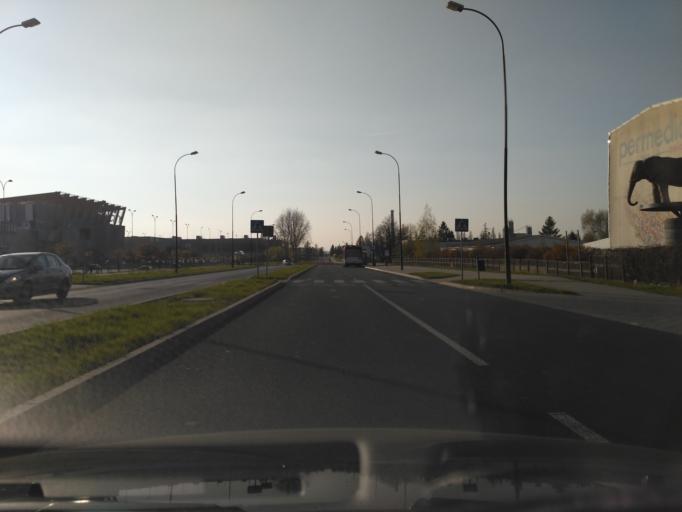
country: PL
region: Lublin Voivodeship
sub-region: Powiat lubelski
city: Jakubowice Murowane
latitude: 51.2326
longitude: 22.6167
